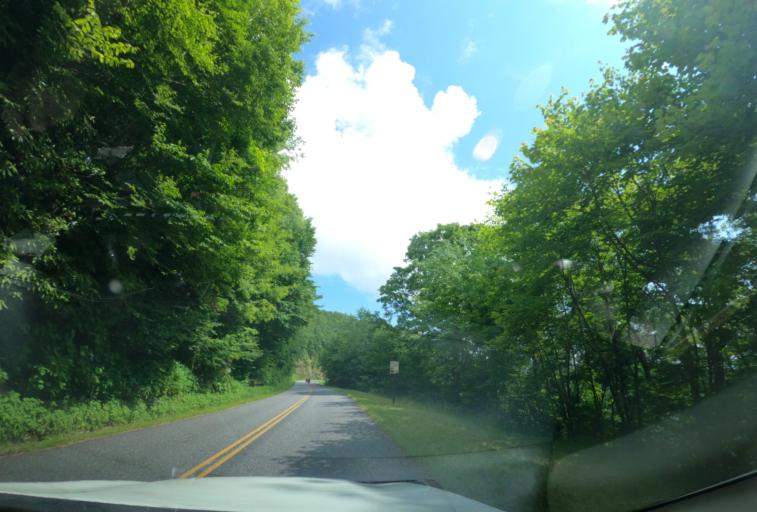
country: US
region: North Carolina
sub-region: Haywood County
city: Hazelwood
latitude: 35.4295
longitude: -83.0356
